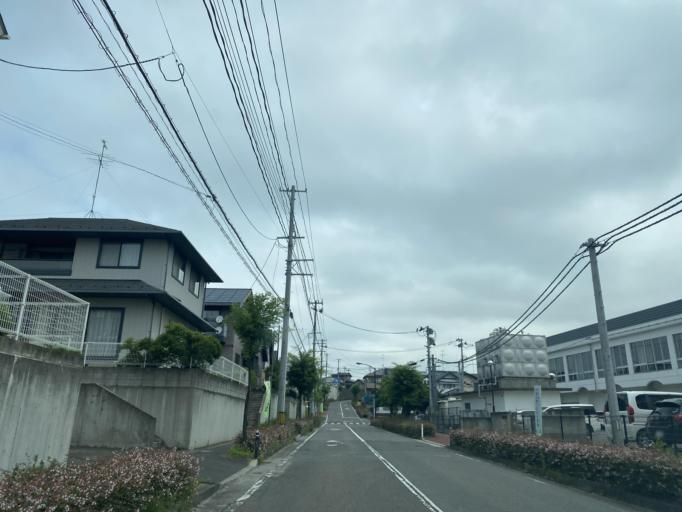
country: JP
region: Fukushima
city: Koriyama
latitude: 37.4310
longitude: 140.3841
